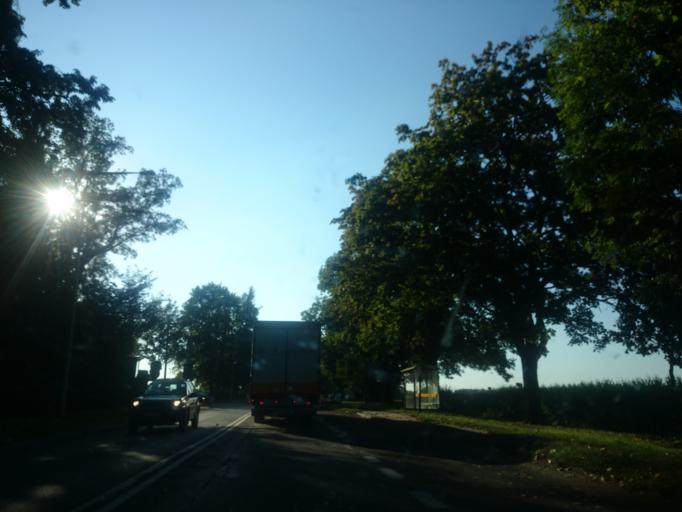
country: PL
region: Lubusz
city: Gorzow Wielkopolski
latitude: 52.7423
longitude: 15.1736
